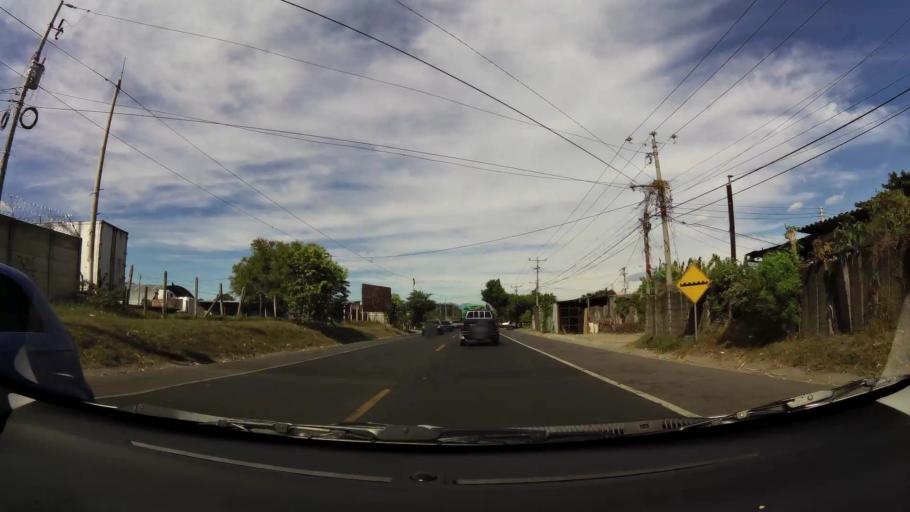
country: SV
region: San Salvador
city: Aguilares
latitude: 13.9446
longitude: -89.1892
